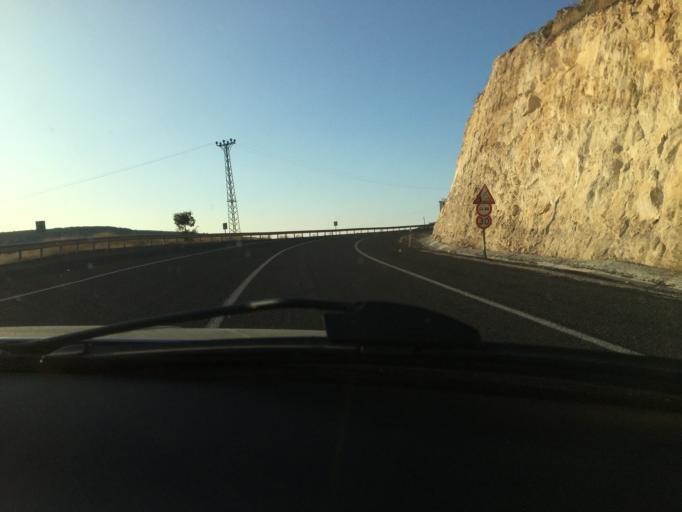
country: TR
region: Sanliurfa
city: Halfeti
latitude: 37.2443
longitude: 37.8735
